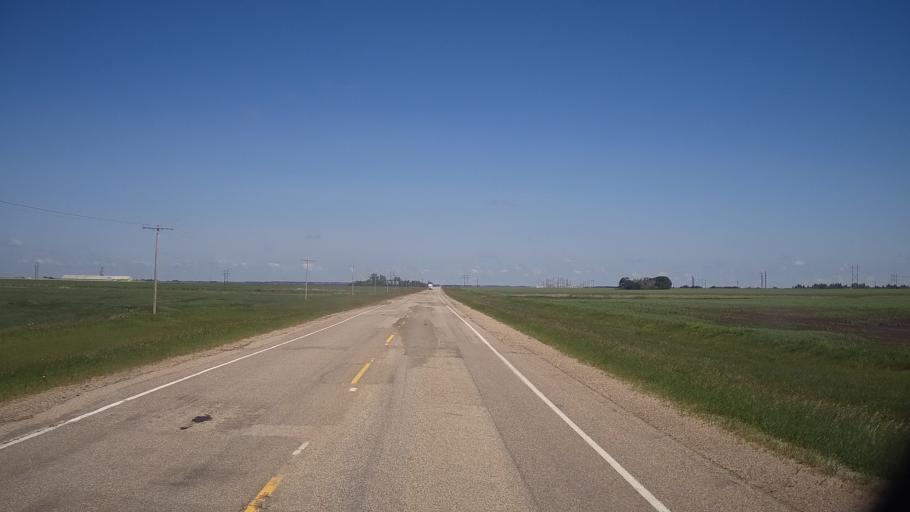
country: CA
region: Saskatchewan
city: Saskatoon
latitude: 51.9702
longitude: -106.0752
